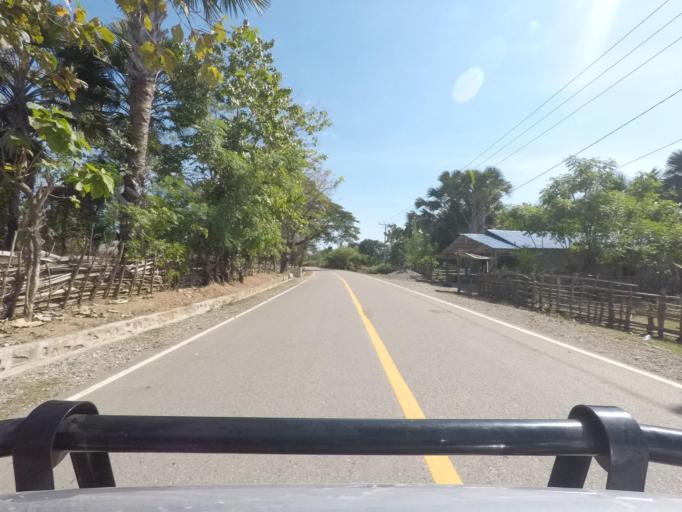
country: TL
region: Bobonaro
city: Maliana
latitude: -8.8798
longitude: 125.0344
